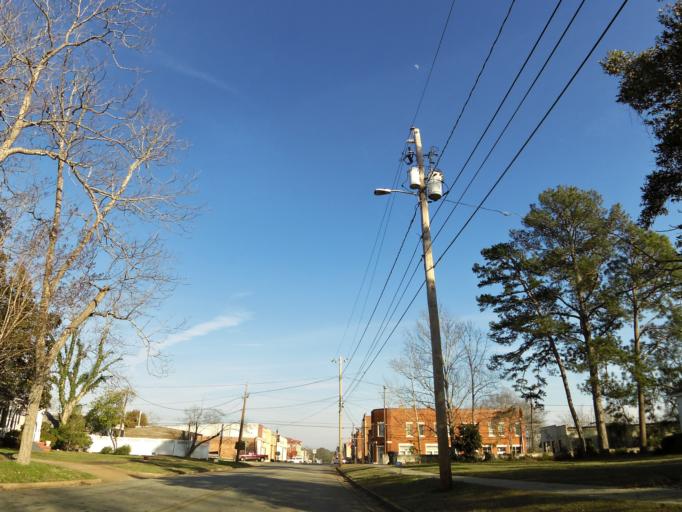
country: US
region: Georgia
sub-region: Stewart County
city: Richland
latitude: 32.0898
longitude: -84.6682
